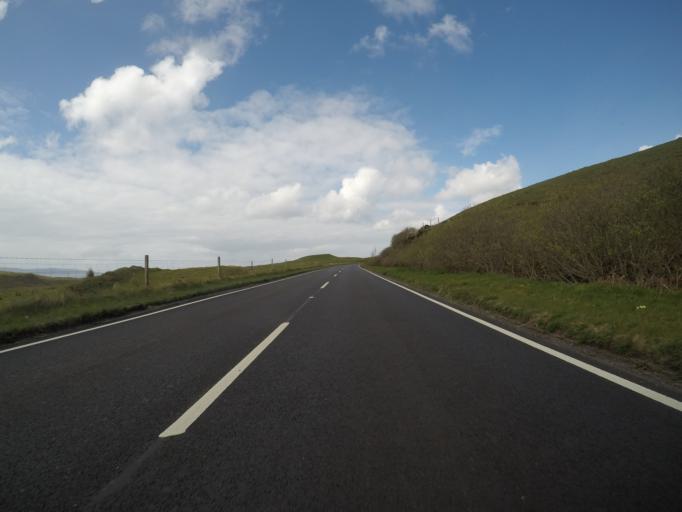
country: GB
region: Scotland
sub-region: Highland
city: Portree
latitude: 57.5414
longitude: -6.3642
